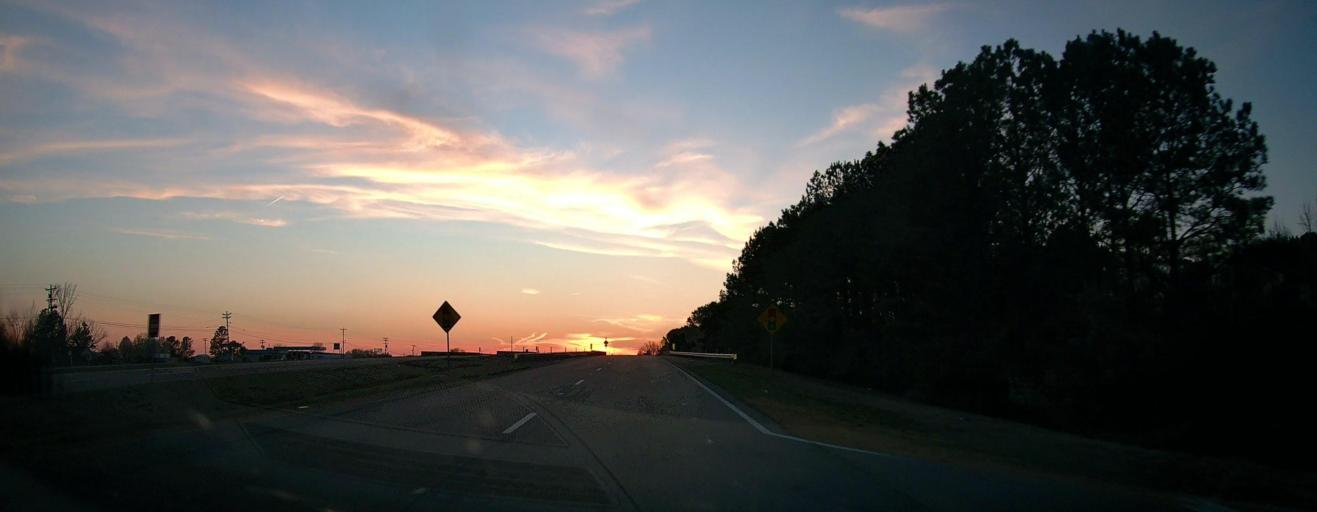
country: US
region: Mississippi
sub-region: Tippah County
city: Ripley
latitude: 34.9526
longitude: -88.8981
